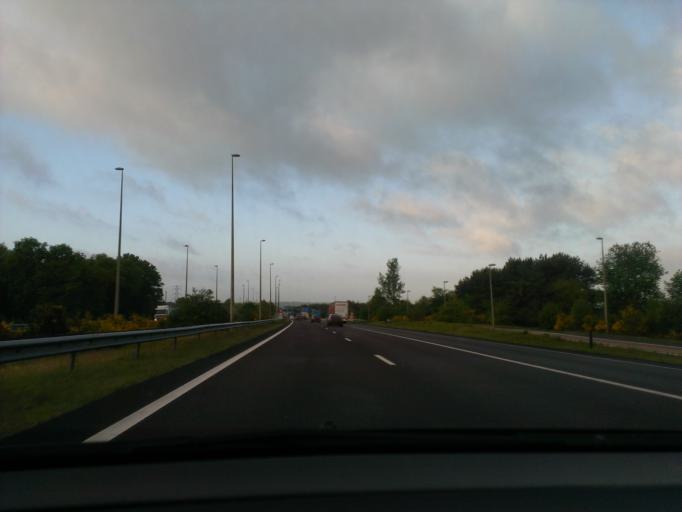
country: NL
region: Gelderland
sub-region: Gemeente Rozendaal
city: Rozendaal
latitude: 52.0598
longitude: 5.9406
